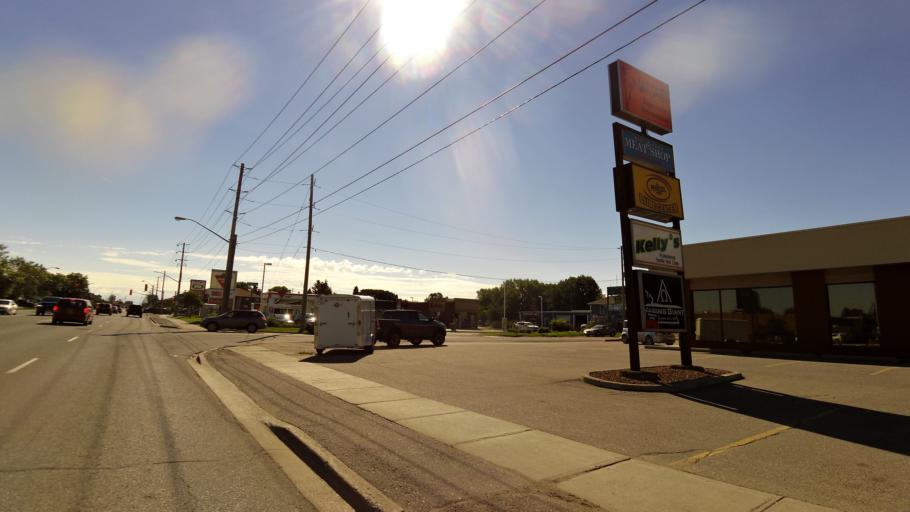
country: CA
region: Ontario
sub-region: Thunder Bay District
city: Thunder Bay
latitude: 48.3807
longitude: -89.2916
